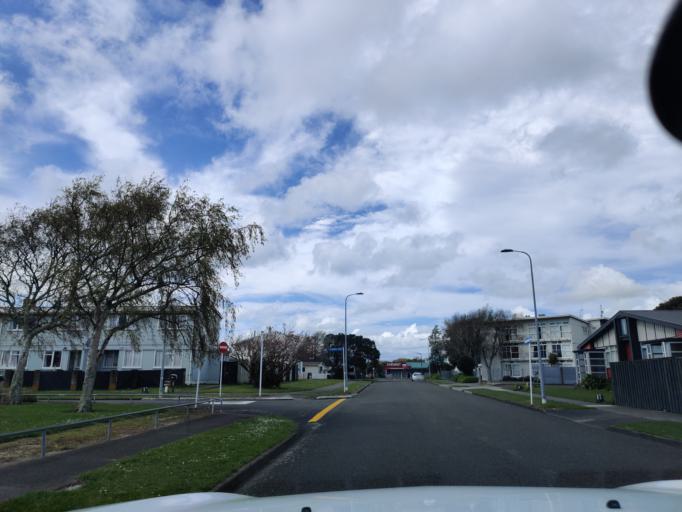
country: NZ
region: Manawatu-Wanganui
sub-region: Palmerston North City
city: Palmerston North
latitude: -40.3576
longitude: 175.5877
